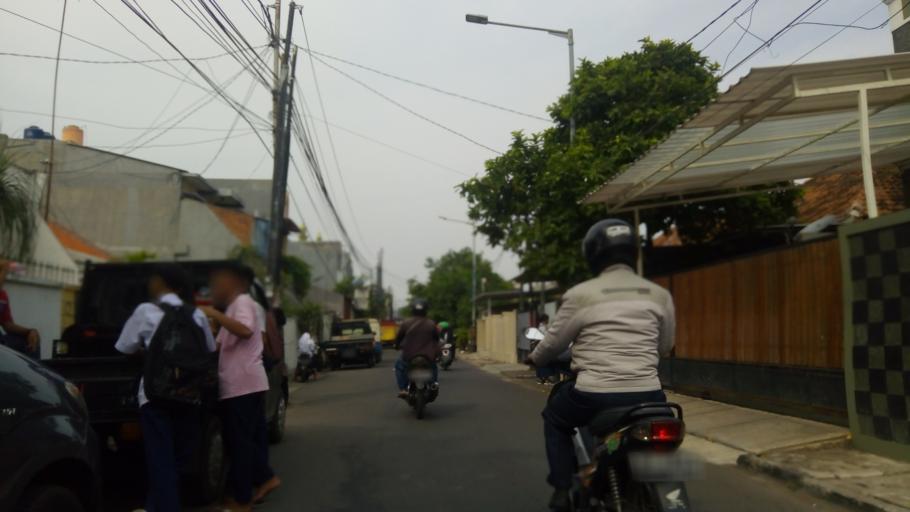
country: ID
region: Jakarta Raya
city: Jakarta
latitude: -6.1717
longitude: 106.8506
